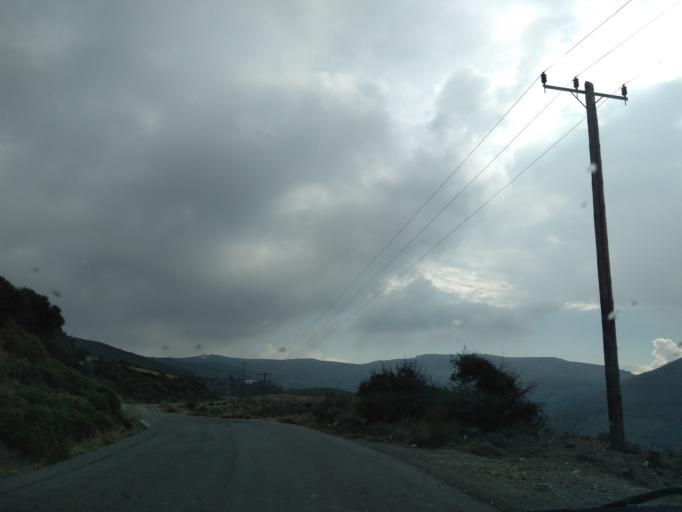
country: GR
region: Crete
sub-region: Nomos Lasithiou
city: Siteia
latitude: 35.1519
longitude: 26.0189
